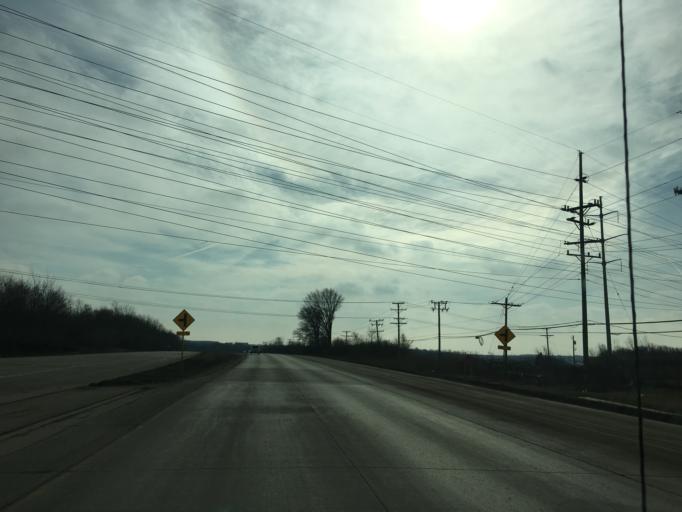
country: US
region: Illinois
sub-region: Kane County
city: East Dundee
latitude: 42.0851
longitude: -88.2386
